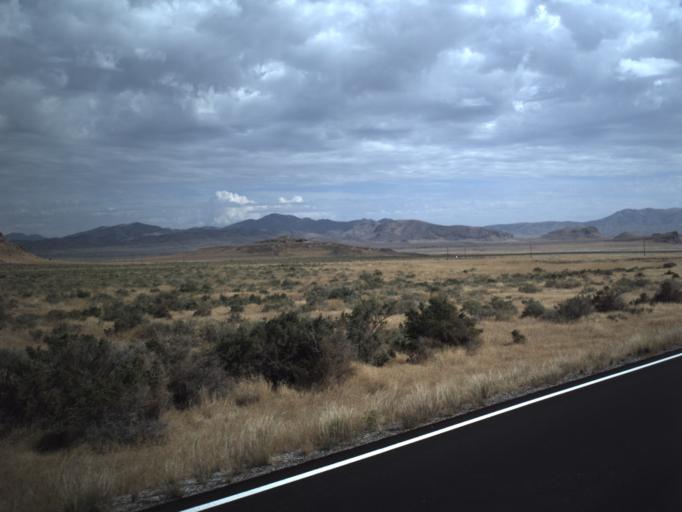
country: US
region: Utah
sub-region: Tooele County
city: Wendover
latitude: 41.4209
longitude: -113.8950
